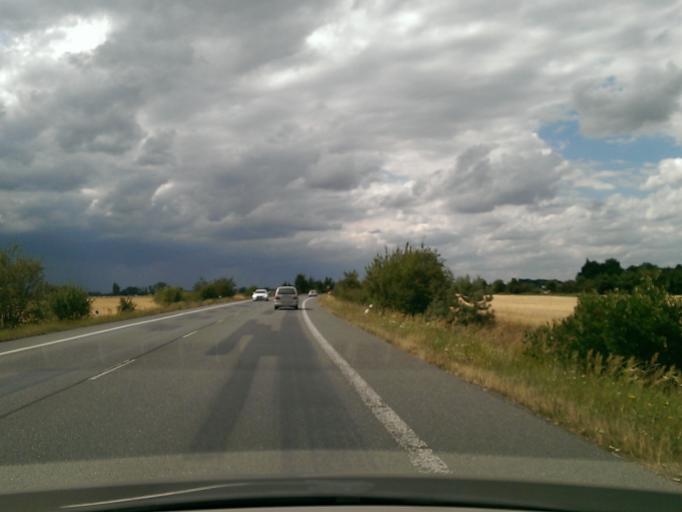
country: CZ
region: Central Bohemia
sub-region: Okres Nymburk
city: Podebrady
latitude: 50.1278
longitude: 15.1045
